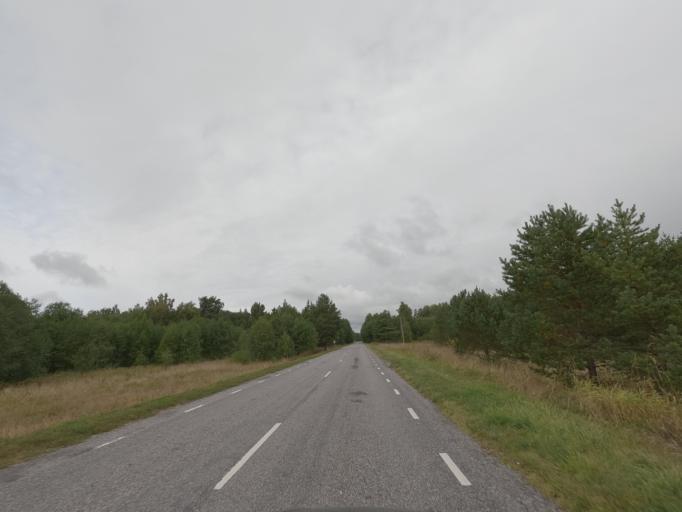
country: EE
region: Raplamaa
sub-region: Maerjamaa vald
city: Marjamaa
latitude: 59.0212
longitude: 24.5593
